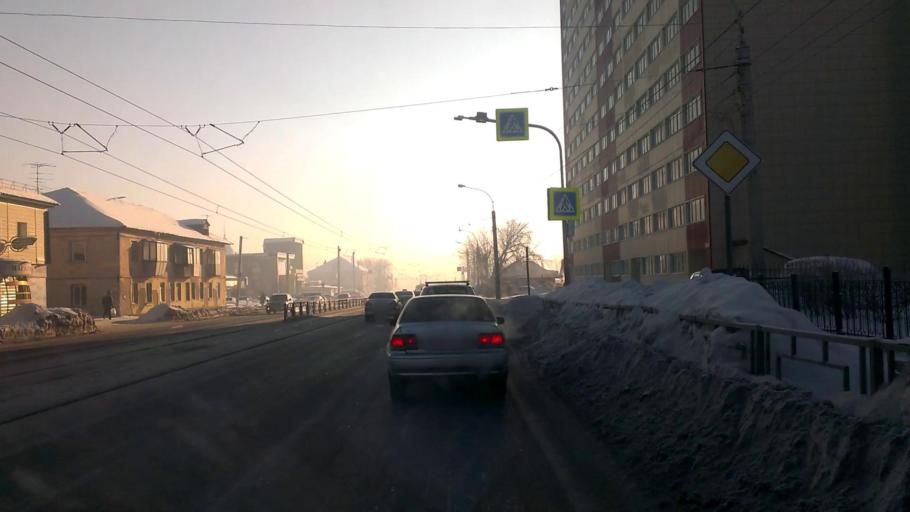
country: RU
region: Altai Krai
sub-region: Gorod Barnaulskiy
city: Barnaul
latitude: 53.3457
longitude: 83.7325
